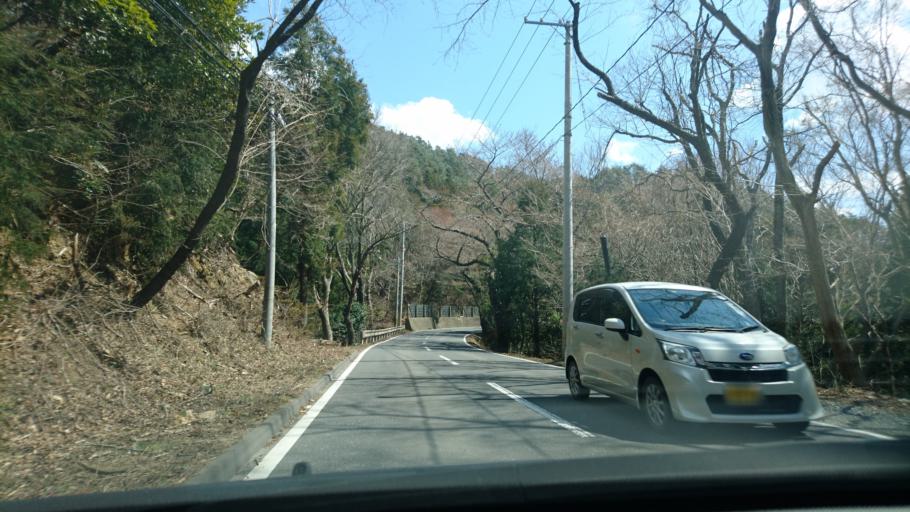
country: JP
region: Miyagi
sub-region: Oshika Gun
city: Onagawa Cho
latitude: 38.4422
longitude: 141.4798
